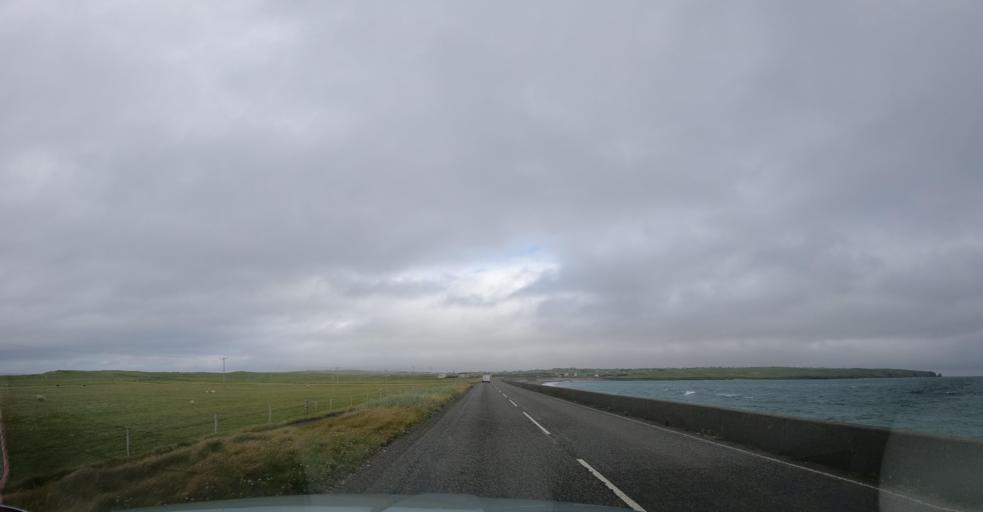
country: GB
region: Scotland
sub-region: Eilean Siar
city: Stornoway
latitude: 58.2053
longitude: -6.2968
